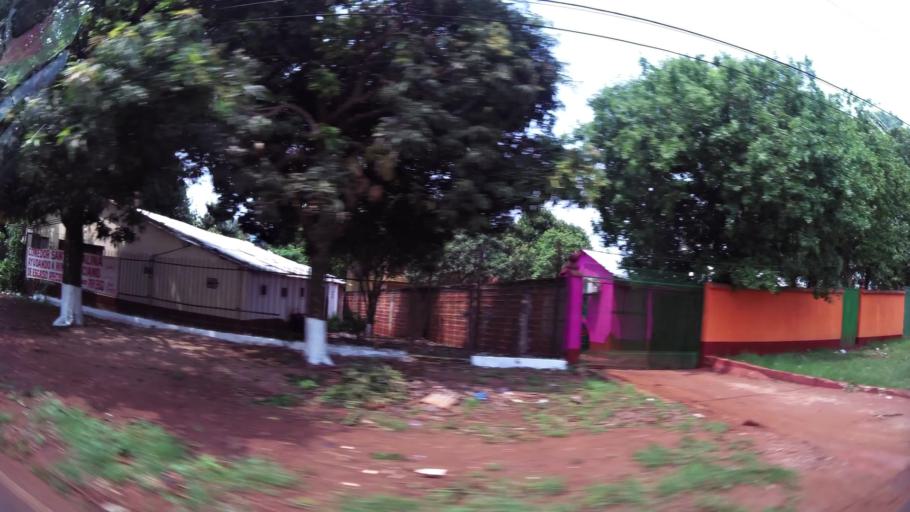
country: BR
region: Parana
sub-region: Foz Do Iguacu
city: Foz do Iguacu
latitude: -25.5696
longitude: -54.6032
